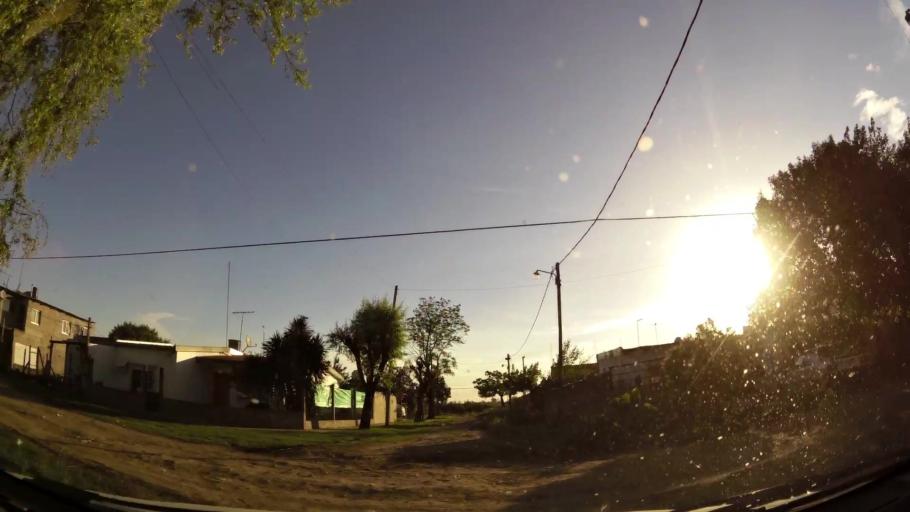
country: AR
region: Buenos Aires
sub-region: Partido de Merlo
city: Merlo
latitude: -34.7002
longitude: -58.7554
